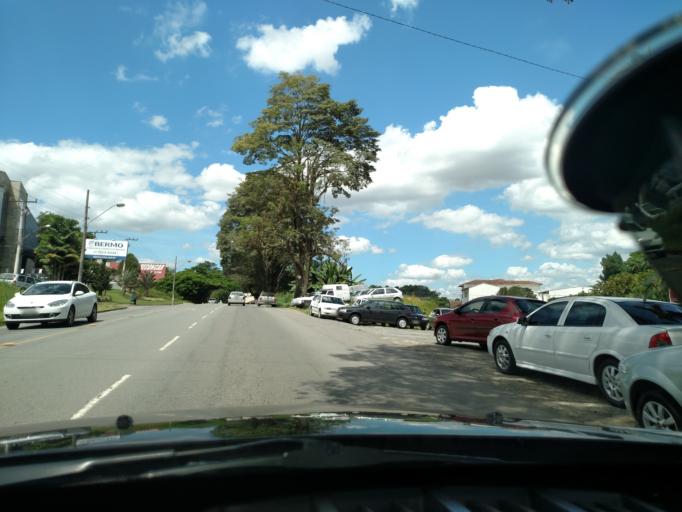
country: BR
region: Santa Catarina
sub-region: Blumenau
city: Blumenau
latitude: -26.8743
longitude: -49.1126
